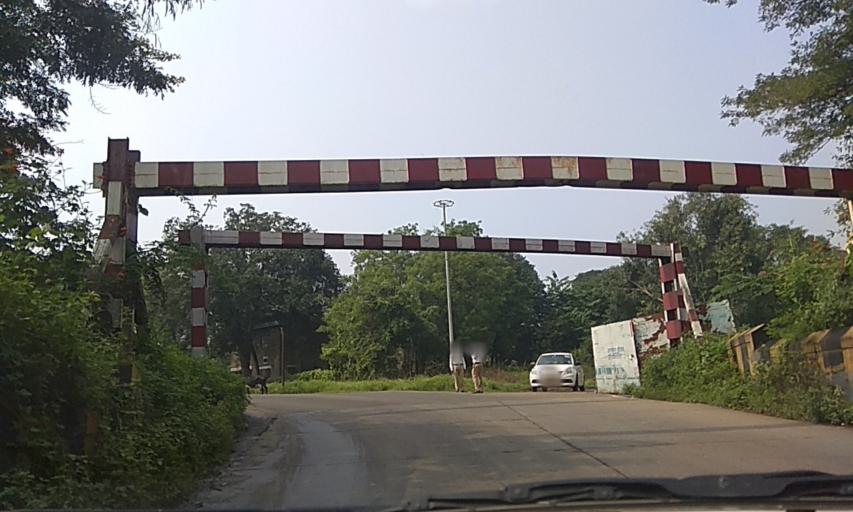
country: IN
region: Maharashtra
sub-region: Pune Division
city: Khadki
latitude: 18.5468
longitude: 73.8472
